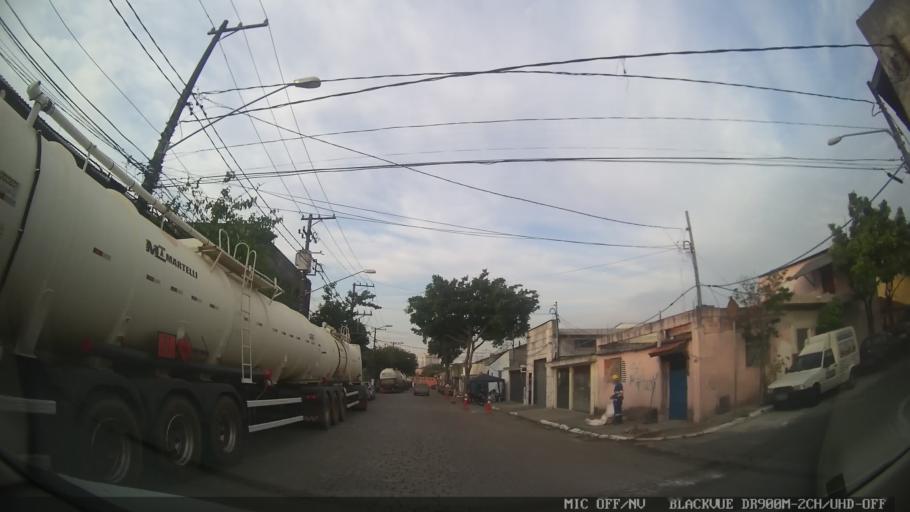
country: BR
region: Sao Paulo
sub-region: Sao Caetano Do Sul
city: Sao Caetano do Sul
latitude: -23.6025
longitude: -46.5849
